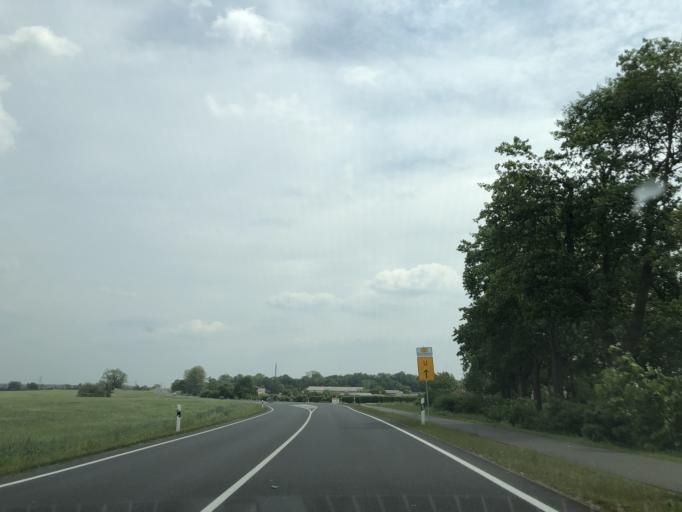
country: DE
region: Brandenburg
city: Kyritz
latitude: 52.9535
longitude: 12.3719
